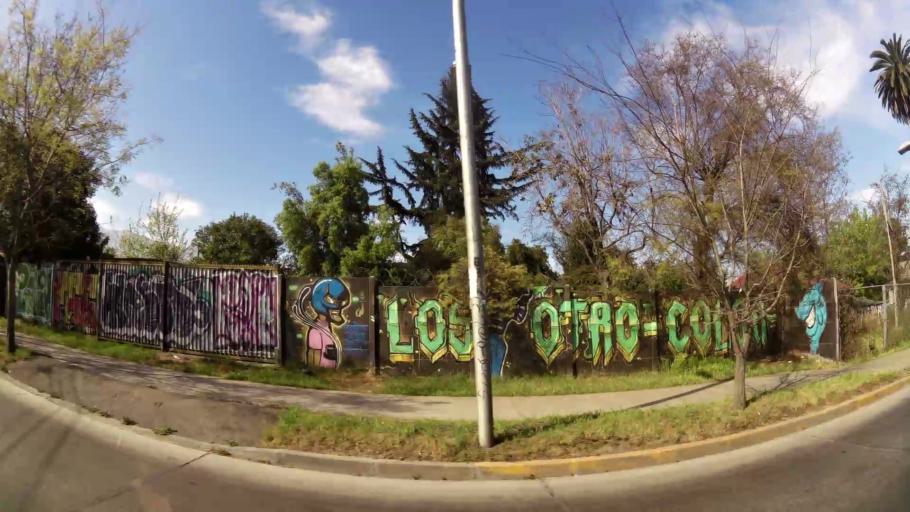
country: CL
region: Santiago Metropolitan
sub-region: Provincia de Santiago
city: Villa Presidente Frei, Nunoa, Santiago, Chile
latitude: -33.4521
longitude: -70.5568
